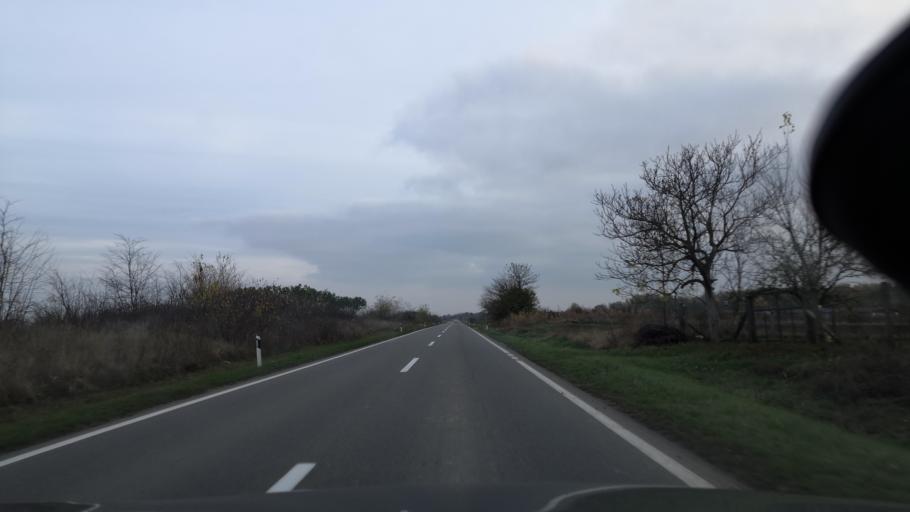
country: RS
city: Sanad
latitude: 45.9934
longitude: 20.1065
